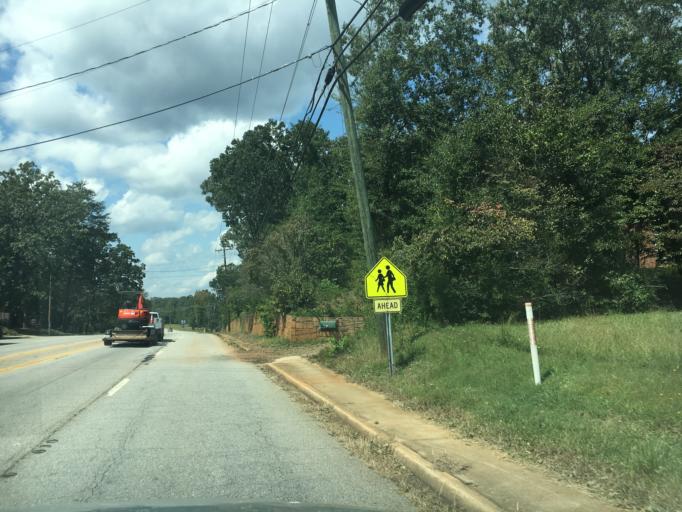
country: US
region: South Carolina
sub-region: Greenville County
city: Berea
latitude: 34.8955
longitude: -82.4721
